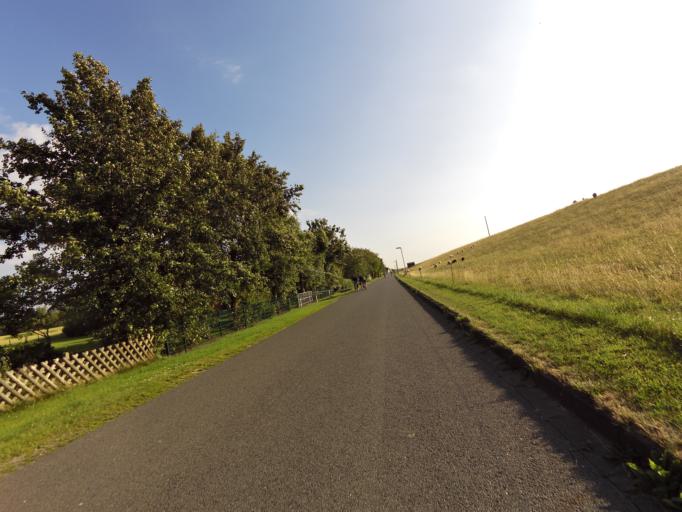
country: DE
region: Lower Saxony
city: Nordholz
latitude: 53.7900
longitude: 8.5558
